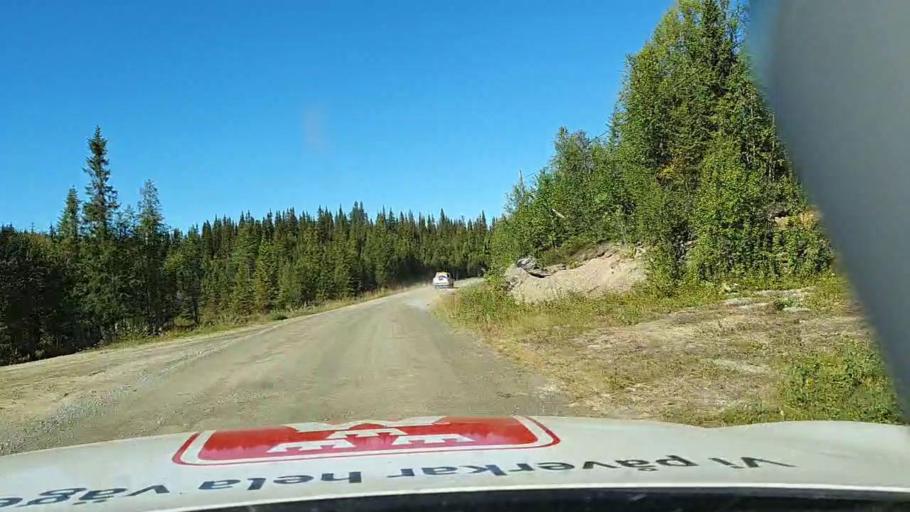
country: SE
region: Vaesterbotten
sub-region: Vilhelmina Kommun
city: Sjoberg
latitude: 65.3076
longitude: 16.1610
